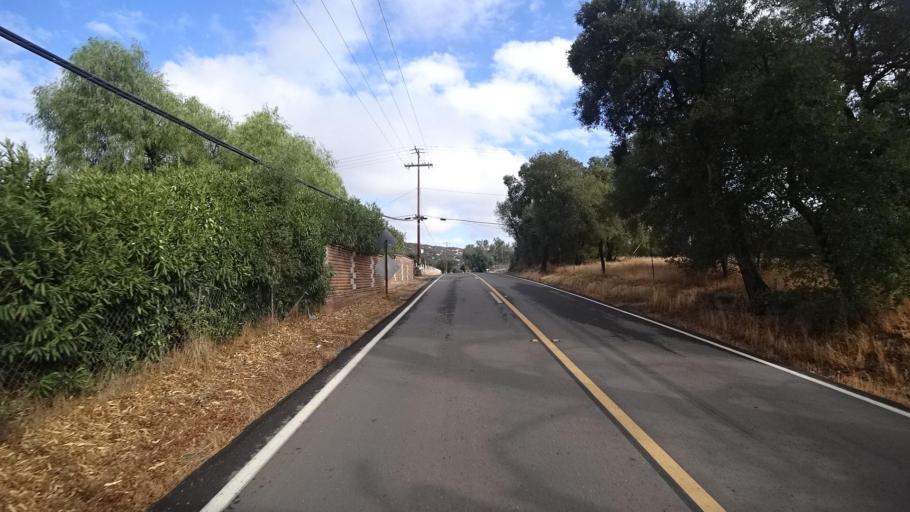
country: MX
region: Baja California
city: Tecate
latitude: 32.6220
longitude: -116.6133
